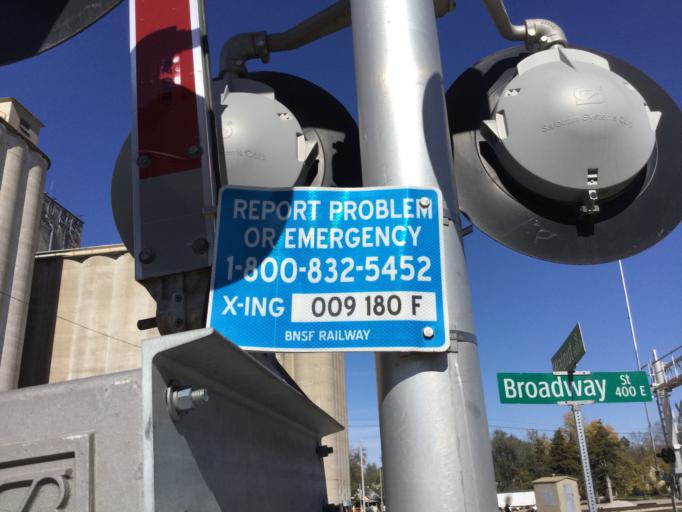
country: US
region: Kansas
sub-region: Harvey County
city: Newton
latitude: 38.0501
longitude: -97.3392
